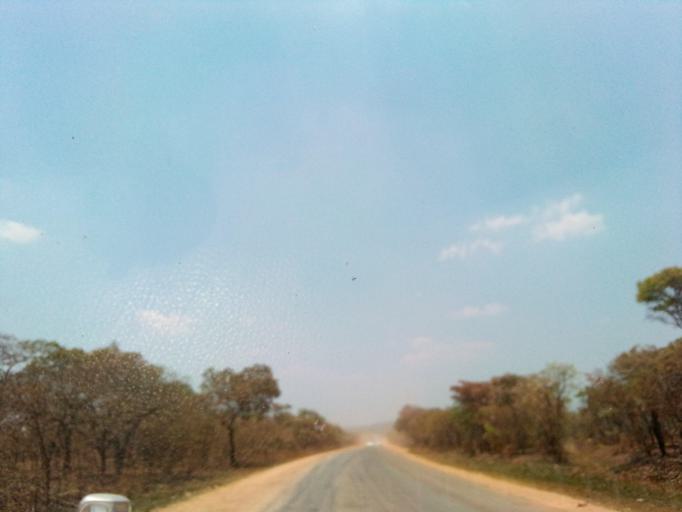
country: ZM
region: Northern
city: Mpika
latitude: -12.2121
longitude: 31.1714
